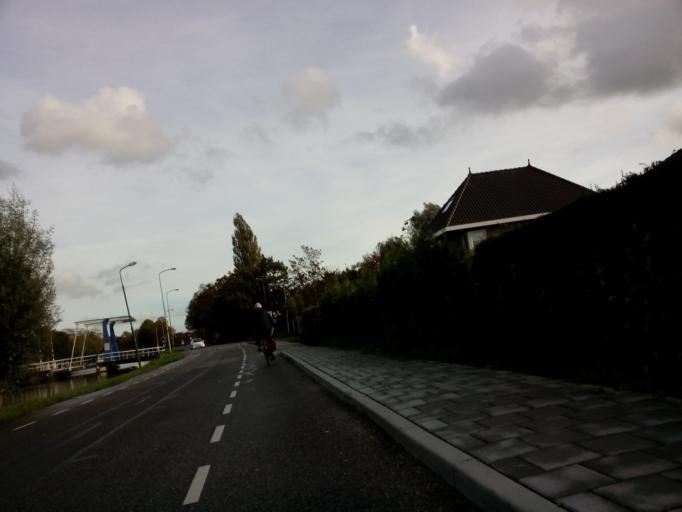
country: NL
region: Utrecht
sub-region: Gemeente Montfoort
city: Montfoort
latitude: 52.0897
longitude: 4.9692
